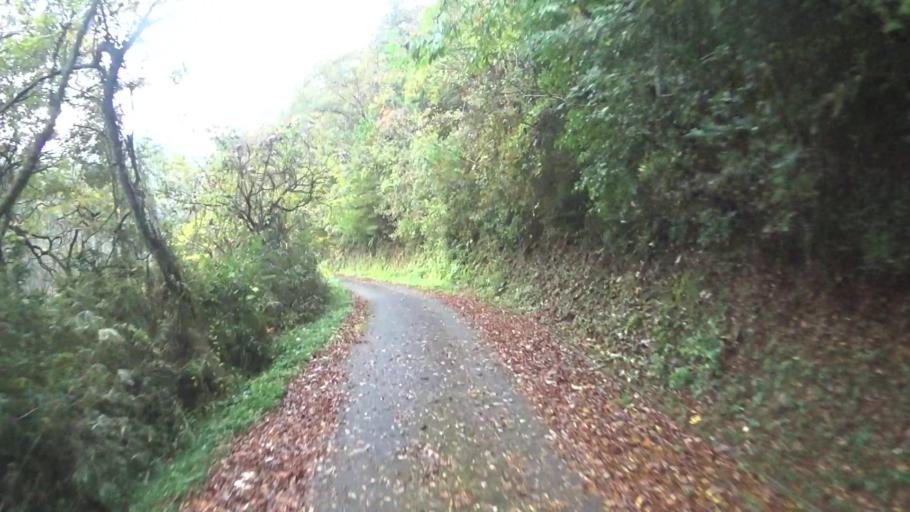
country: JP
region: Kyoto
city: Ayabe
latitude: 35.2633
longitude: 135.2254
